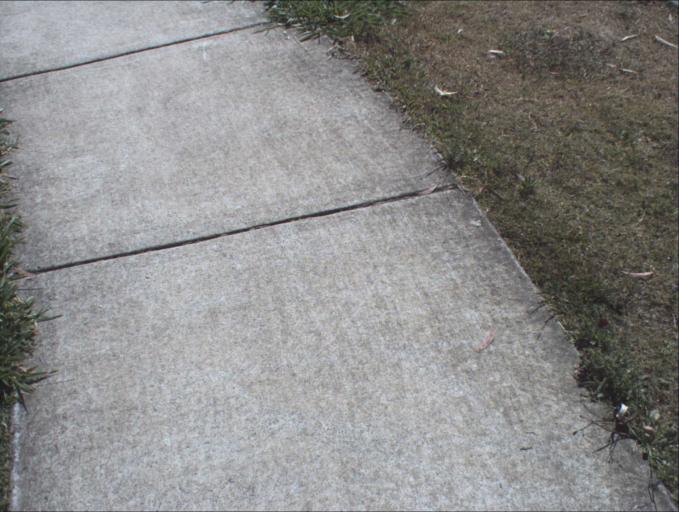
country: AU
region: Queensland
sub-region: Gold Coast
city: Yatala
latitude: -27.7063
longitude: 153.2272
